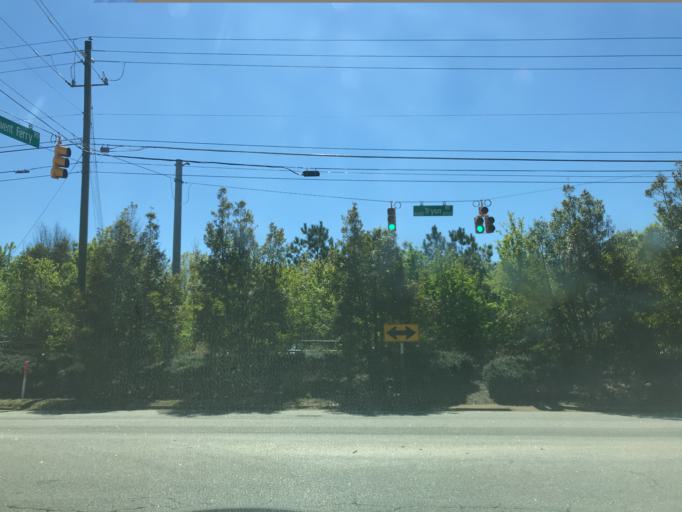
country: US
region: North Carolina
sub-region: Wake County
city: West Raleigh
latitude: 35.7489
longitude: -78.7177
